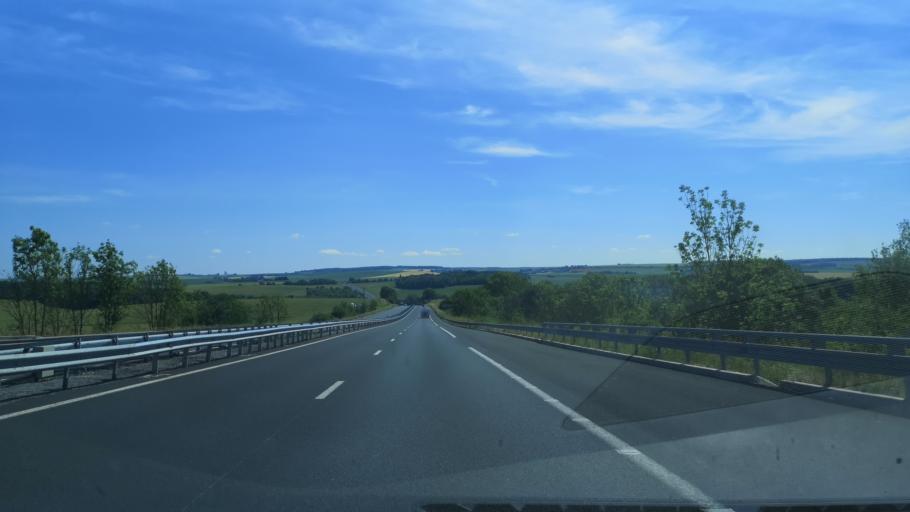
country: FR
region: Champagne-Ardenne
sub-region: Departement de la Marne
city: Dormans
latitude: 49.1489
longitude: 3.6729
